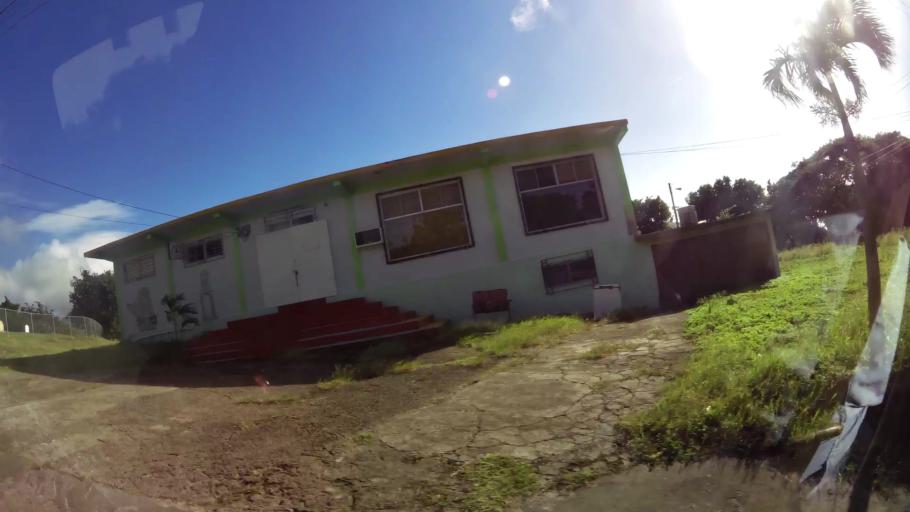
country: MS
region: Saint Peter
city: Saint Peters
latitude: 16.7484
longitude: -62.2206
